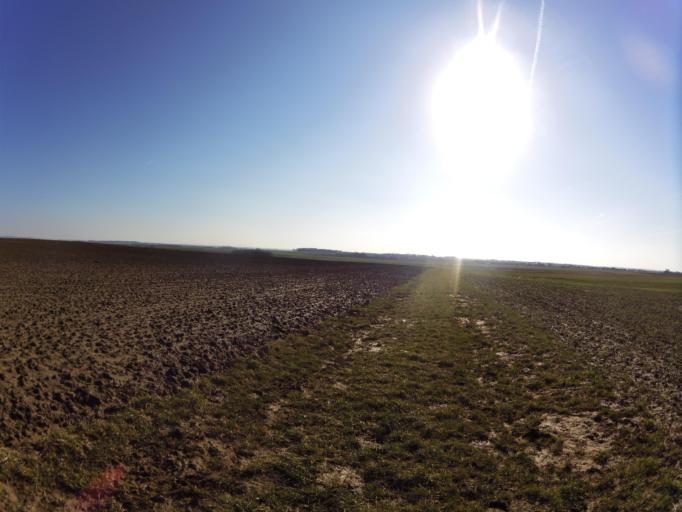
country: DE
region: Bavaria
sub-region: Regierungsbezirk Unterfranken
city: Giebelstadt
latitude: 49.6847
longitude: 9.9700
